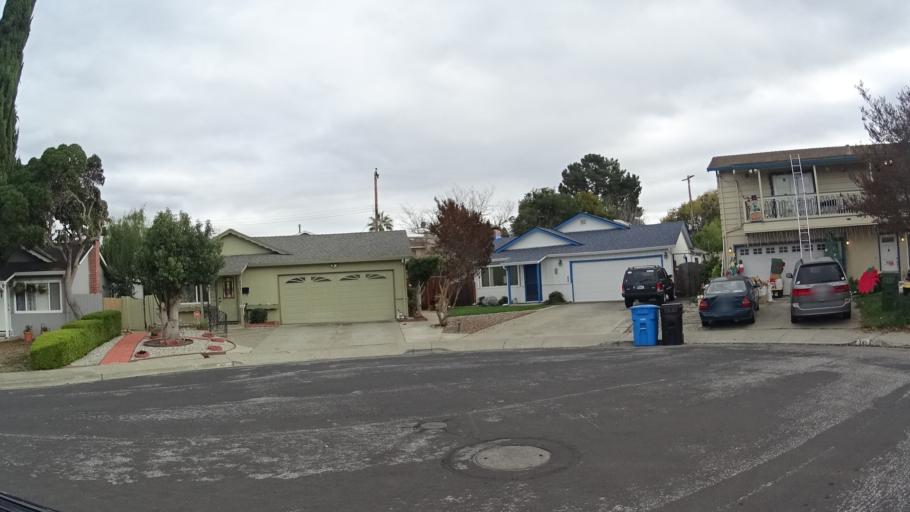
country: US
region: California
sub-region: Santa Clara County
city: Santa Clara
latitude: 37.3297
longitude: -121.9854
